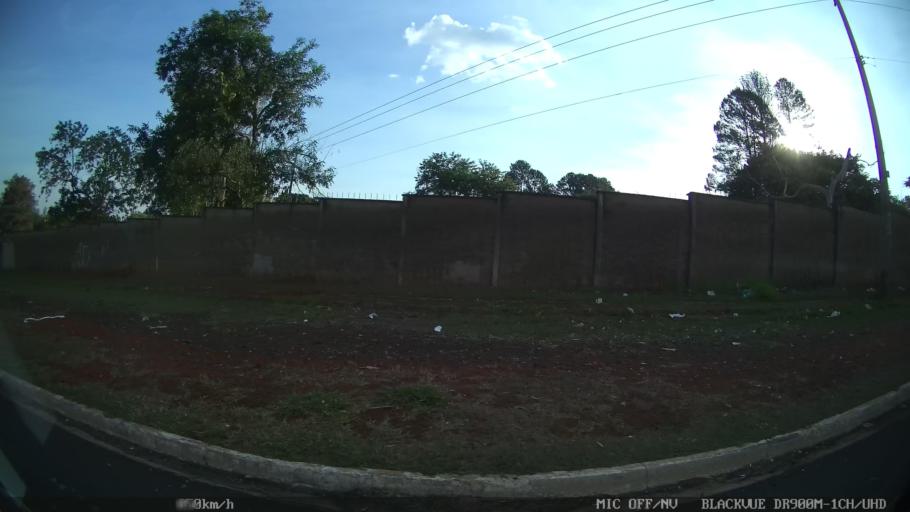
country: BR
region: Sao Paulo
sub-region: Ribeirao Preto
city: Ribeirao Preto
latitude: -21.1683
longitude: -47.8466
